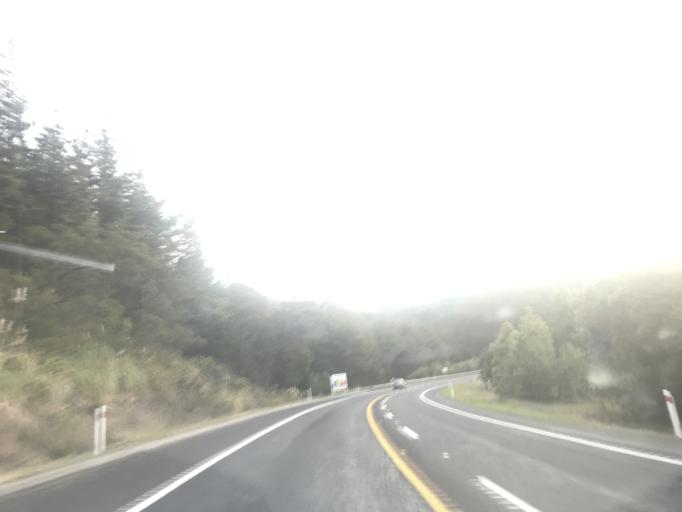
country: NZ
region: Bay of Plenty
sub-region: Western Bay of Plenty District
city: Waihi Beach
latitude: -37.4623
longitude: 175.9174
